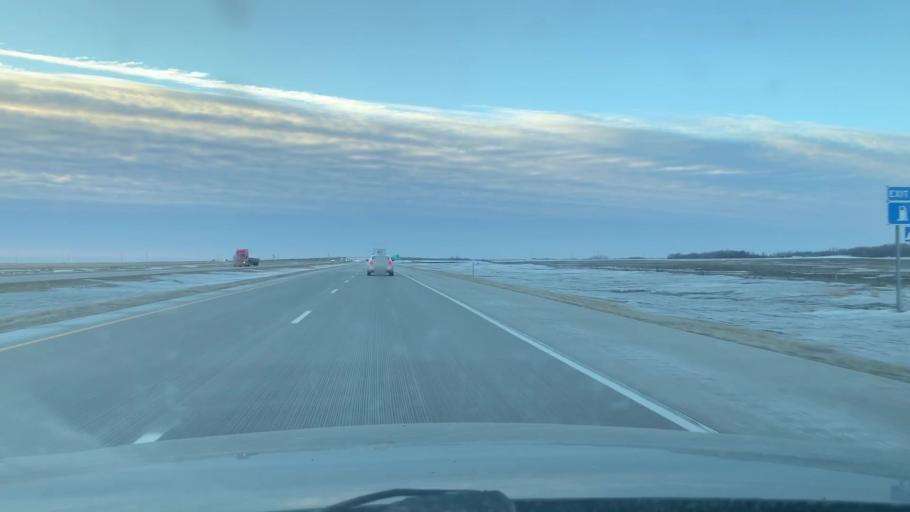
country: US
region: North Dakota
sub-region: Ransom County
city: Sheldon
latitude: 46.8758
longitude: -97.5381
